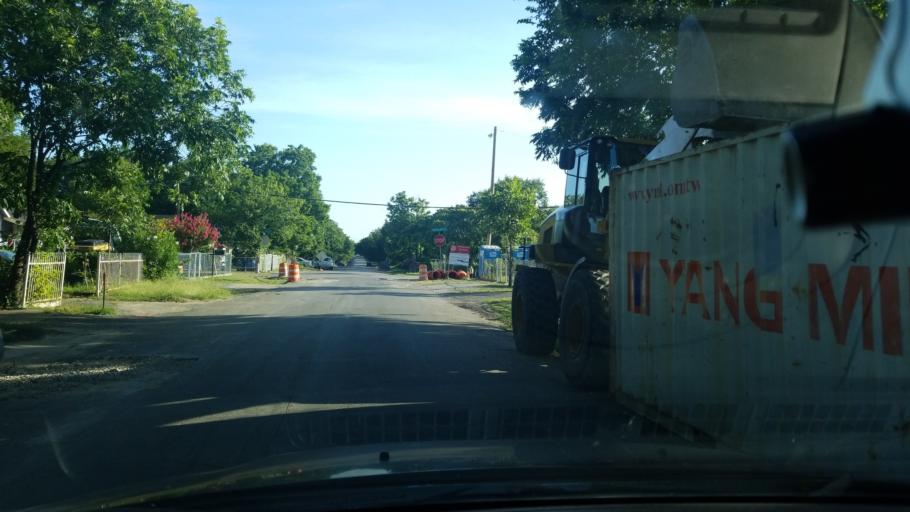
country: US
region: Texas
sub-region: Dallas County
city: Dallas
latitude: 32.7145
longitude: -96.8170
